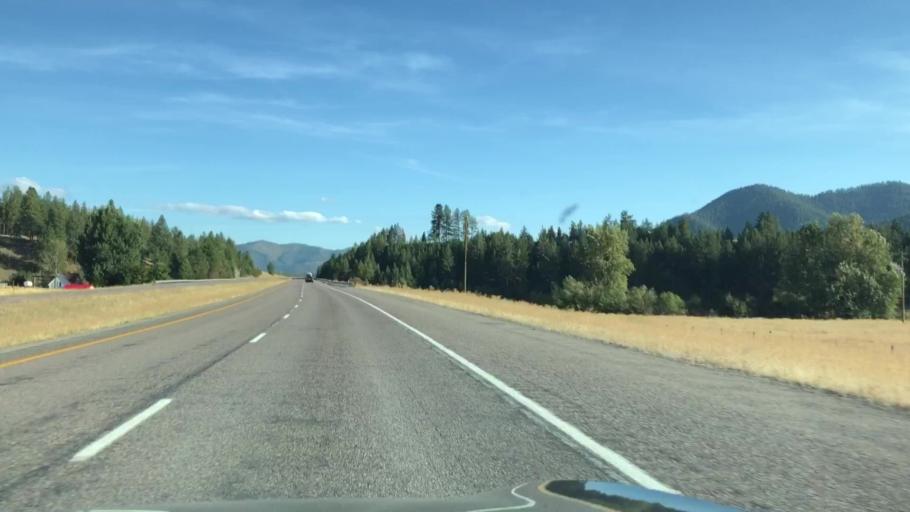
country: US
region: Montana
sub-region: Mineral County
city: Superior
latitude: 47.0556
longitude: -114.7609
